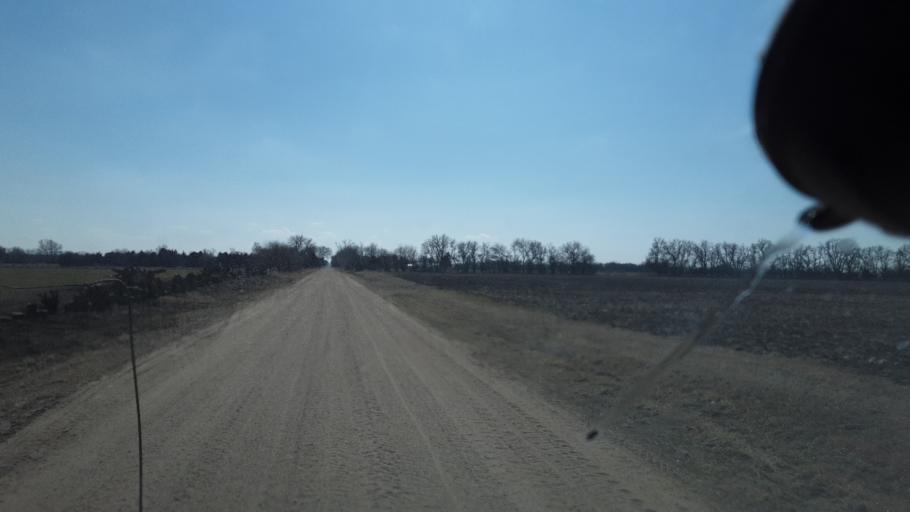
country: US
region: Kansas
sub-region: Reno County
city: Haven
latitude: 37.9218
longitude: -97.8485
